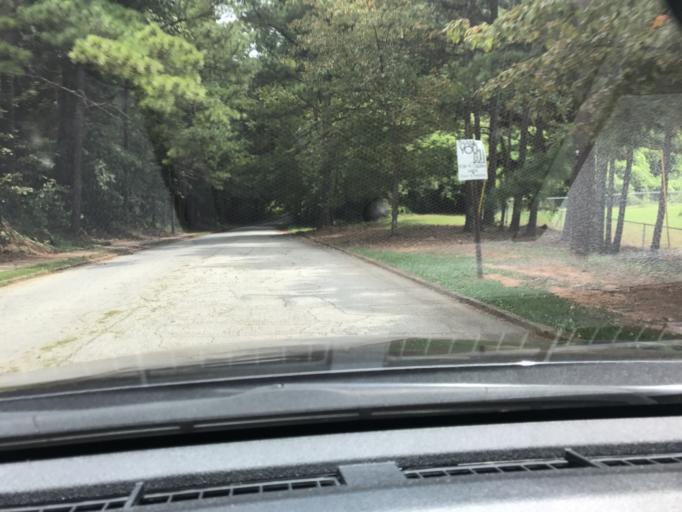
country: US
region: Georgia
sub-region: DeKalb County
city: Belvedere Park
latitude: 33.7468
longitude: -84.2460
